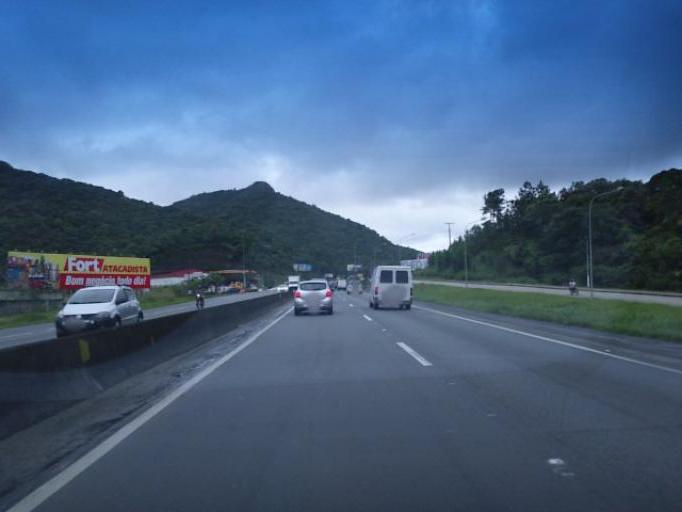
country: BR
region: Santa Catarina
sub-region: Balneario Camboriu
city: Balneario Camboriu
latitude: -26.9829
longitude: -48.6728
